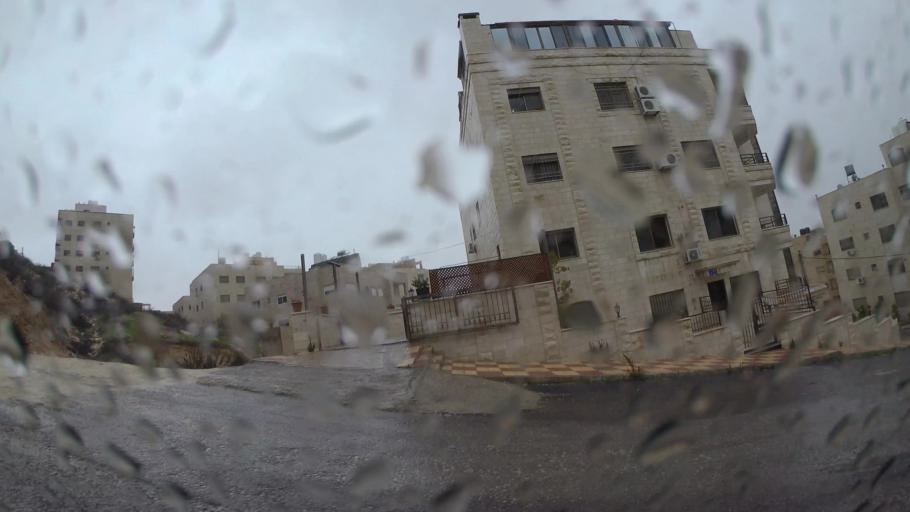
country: JO
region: Amman
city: Al Jubayhah
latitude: 32.0196
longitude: 35.8905
